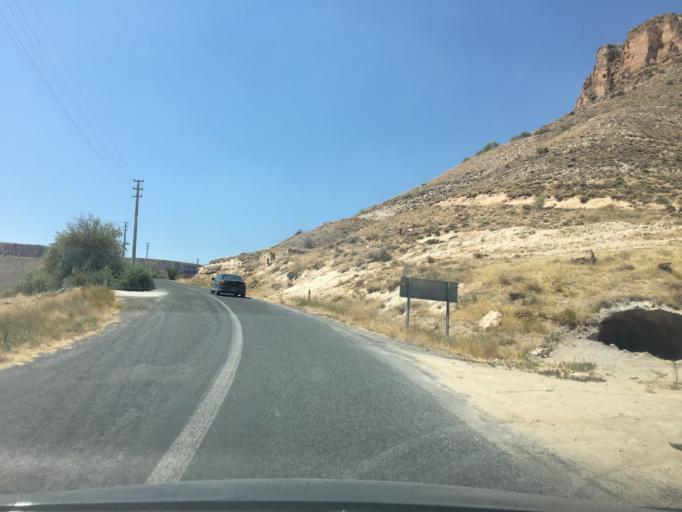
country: TR
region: Nevsehir
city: Urgub
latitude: 38.4710
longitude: 34.9474
